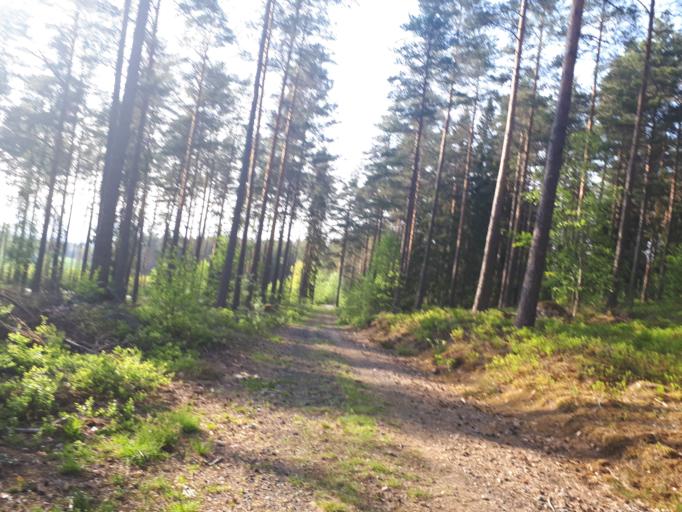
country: SE
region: Soedermanland
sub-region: Flens Kommun
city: Halleforsnas
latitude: 59.0665
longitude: 16.3962
